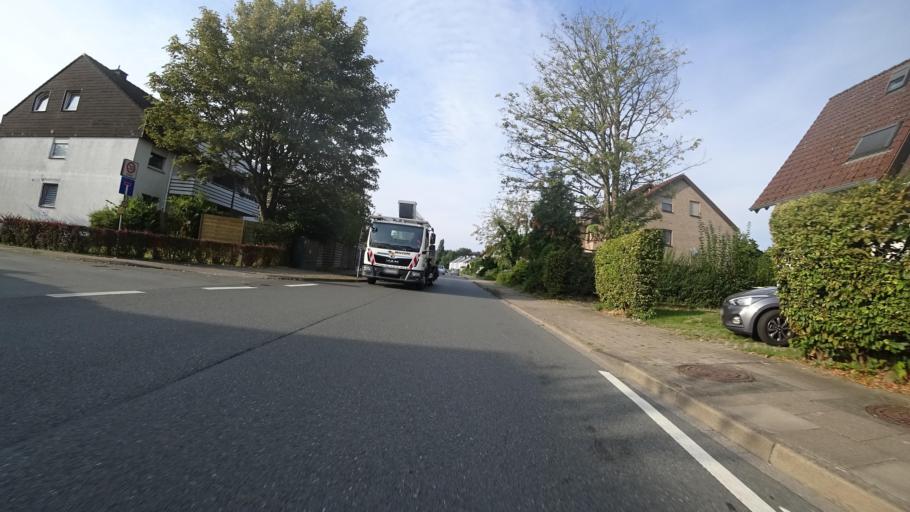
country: DE
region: North Rhine-Westphalia
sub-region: Regierungsbezirk Detmold
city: Werther
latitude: 52.0369
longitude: 8.4635
